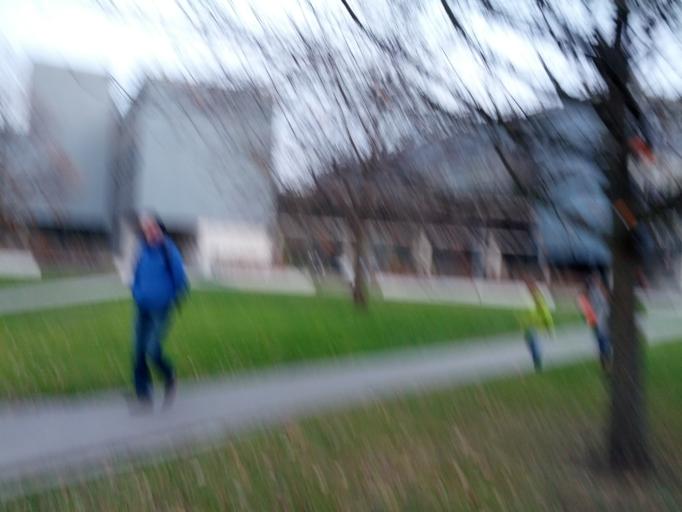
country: DE
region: Baden-Wuerttemberg
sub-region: Freiburg Region
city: Freiburg
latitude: 48.0135
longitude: 7.8341
